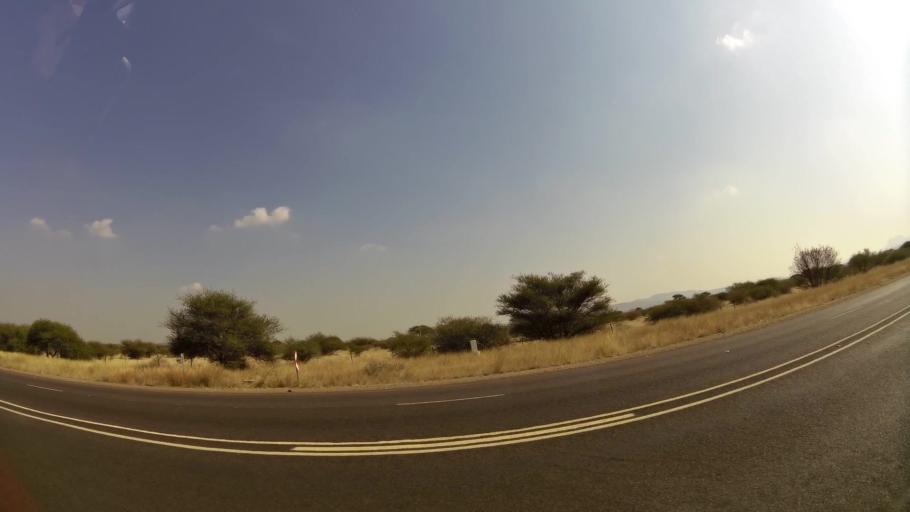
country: ZA
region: North-West
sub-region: Bojanala Platinum District Municipality
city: Mogwase
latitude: -25.4031
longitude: 27.0739
